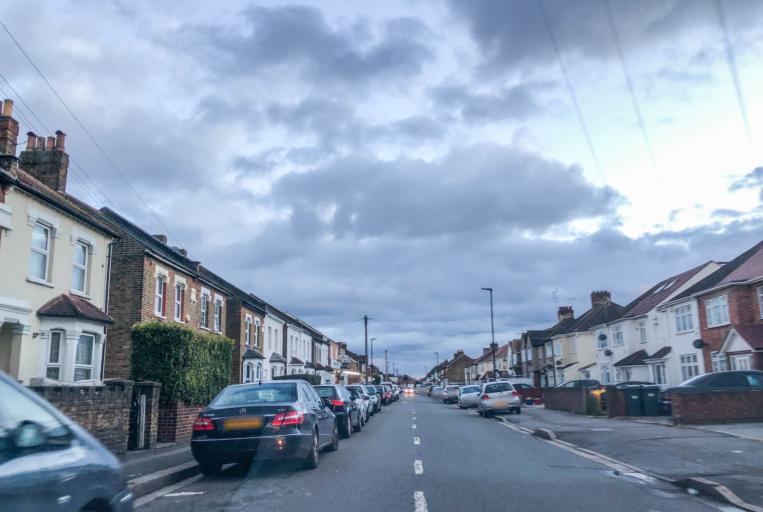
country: GB
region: England
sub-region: Greater London
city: Hounslow
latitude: 51.4637
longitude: -0.3728
